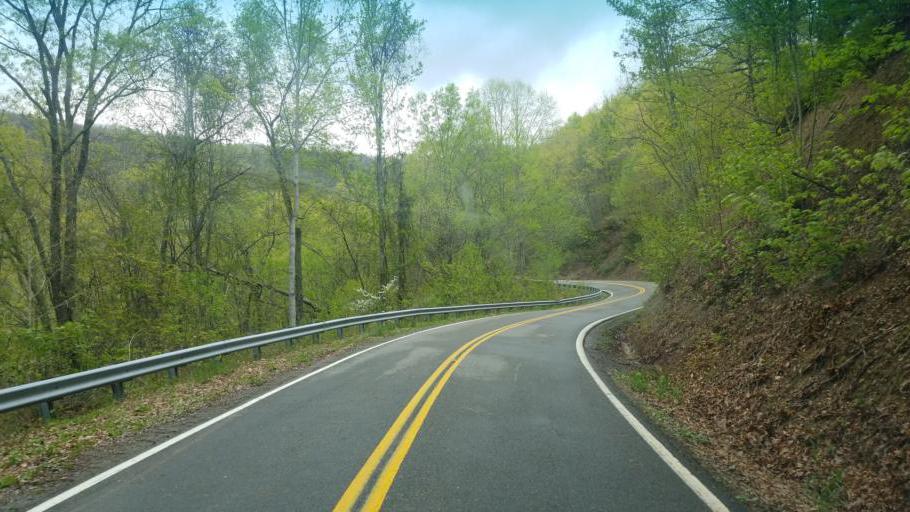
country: US
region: Virginia
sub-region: Tazewell County
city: Tazewell
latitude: 37.0107
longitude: -81.5197
